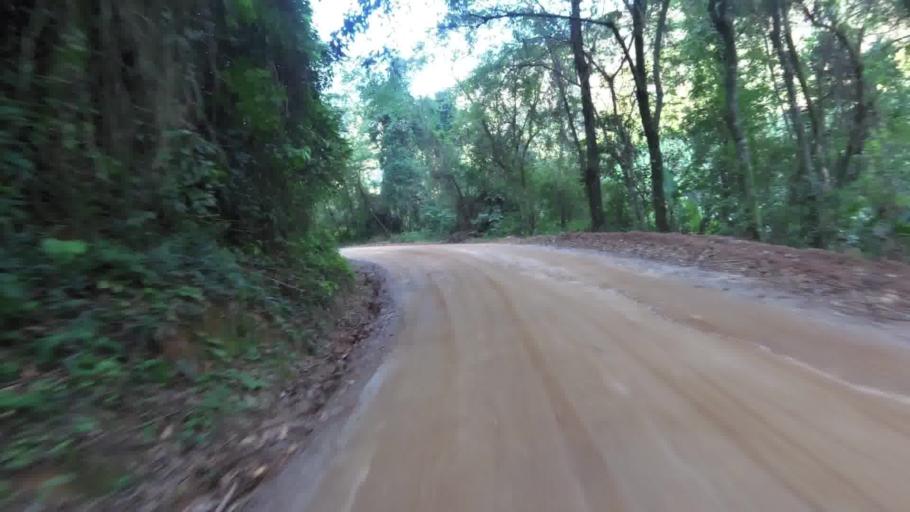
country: BR
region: Espirito Santo
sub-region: Alfredo Chaves
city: Alfredo Chaves
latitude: -20.5676
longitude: -40.6945
